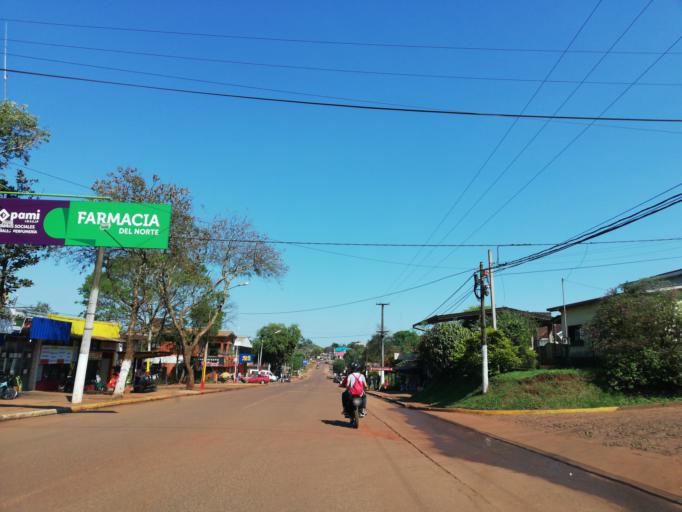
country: AR
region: Misiones
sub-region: Departamento de Eldorado
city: Eldorado
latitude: -26.4067
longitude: -54.6579
